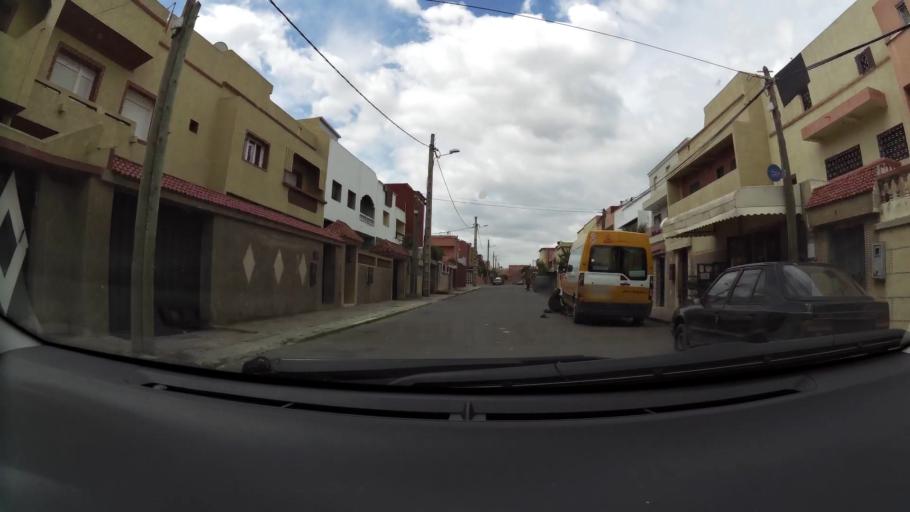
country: MA
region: Grand Casablanca
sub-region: Casablanca
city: Casablanca
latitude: 33.6119
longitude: -7.5460
